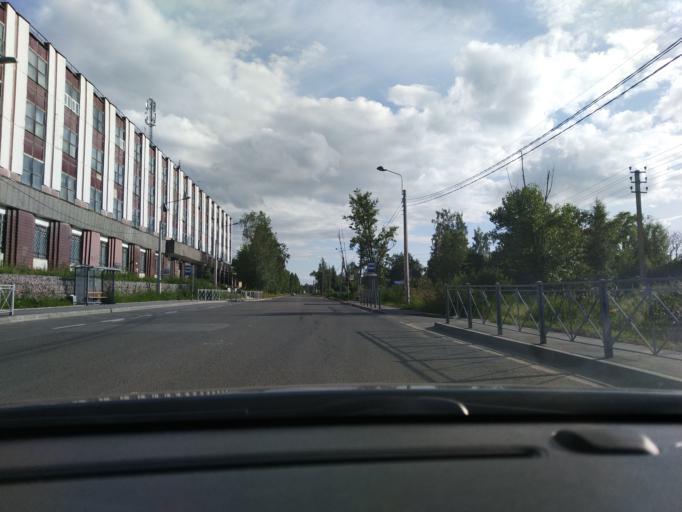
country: RU
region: St.-Petersburg
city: Gorelovo
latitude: 59.7805
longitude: 30.1494
